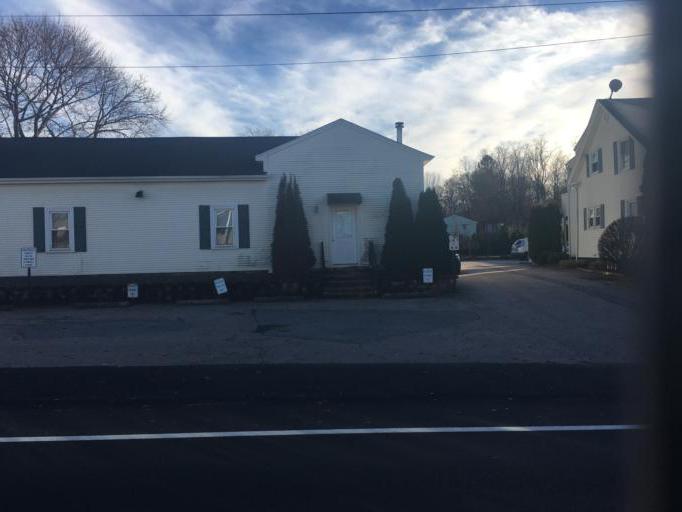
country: US
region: Rhode Island
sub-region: Kent County
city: West Warwick
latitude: 41.6960
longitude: -71.5178
